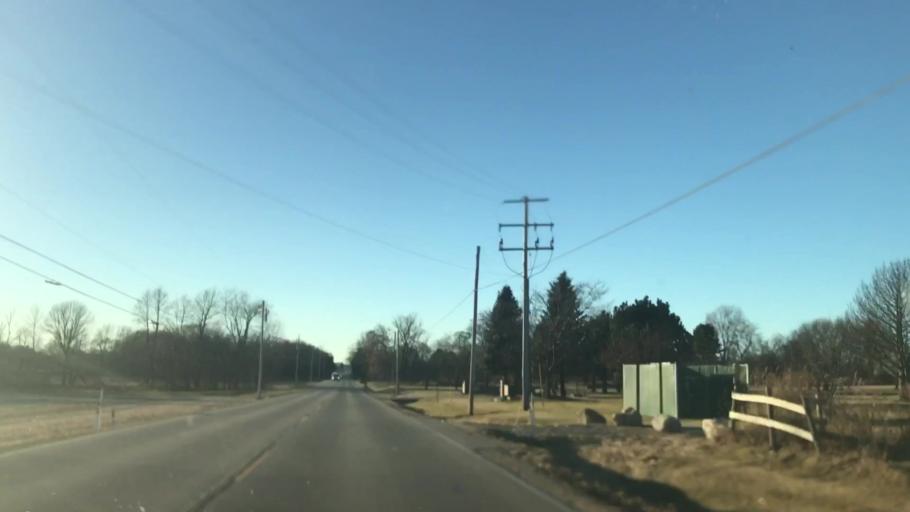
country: US
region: Wisconsin
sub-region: Washington County
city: Jackson
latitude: 43.2945
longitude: -88.1304
